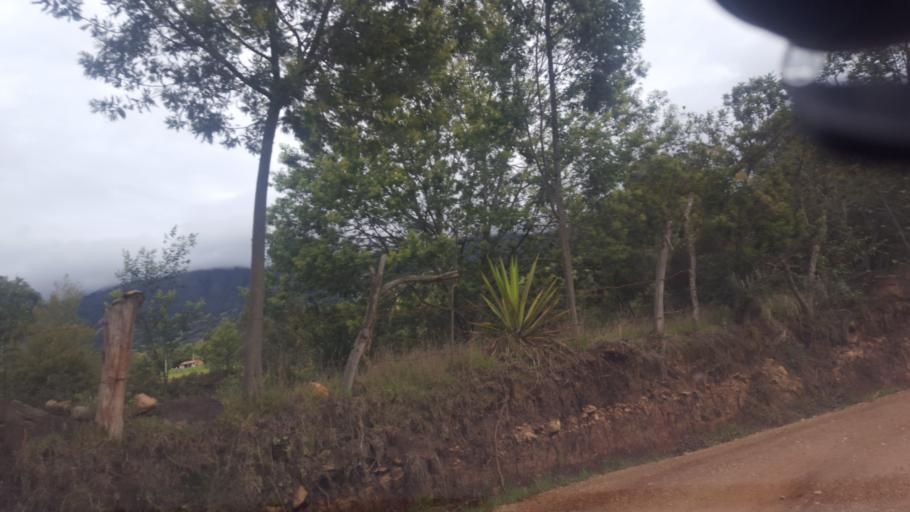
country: CO
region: Boyaca
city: Cerinza
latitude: 5.9883
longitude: -72.9491
